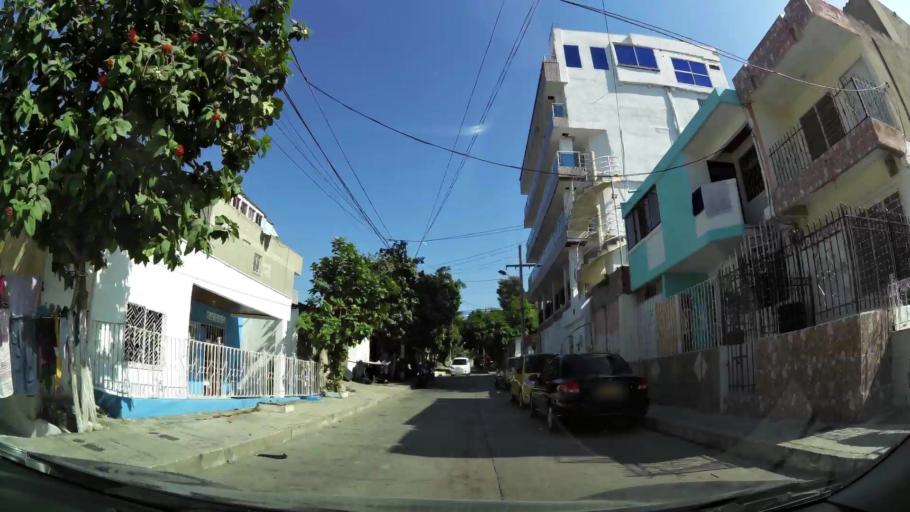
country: CO
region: Bolivar
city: Cartagena
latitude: 10.4016
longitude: -75.4956
